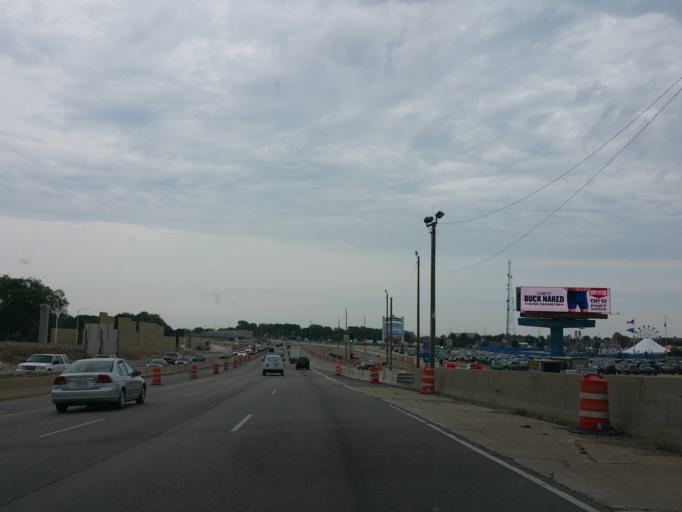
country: US
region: Wisconsin
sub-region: Milwaukee County
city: West Allis
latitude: 43.0272
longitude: -88.0165
